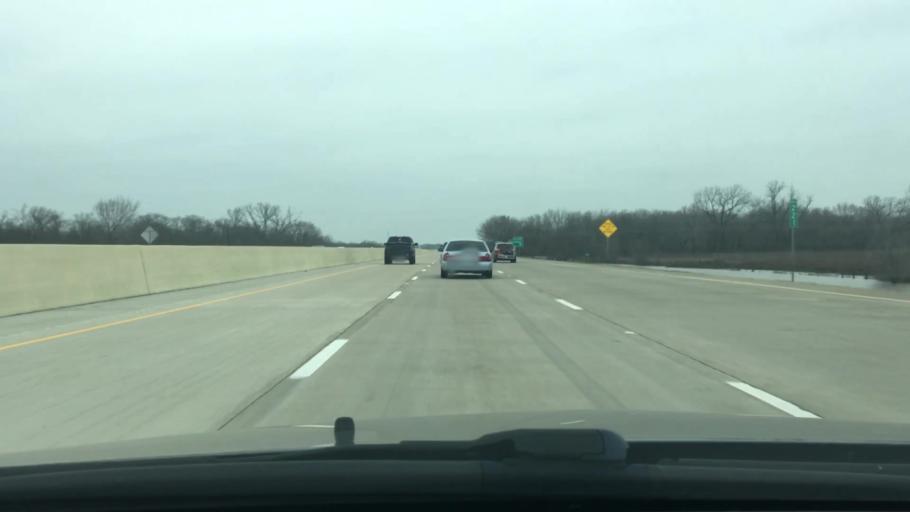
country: US
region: Texas
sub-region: Navarro County
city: Corsicana
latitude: 31.9526
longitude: -96.4214
